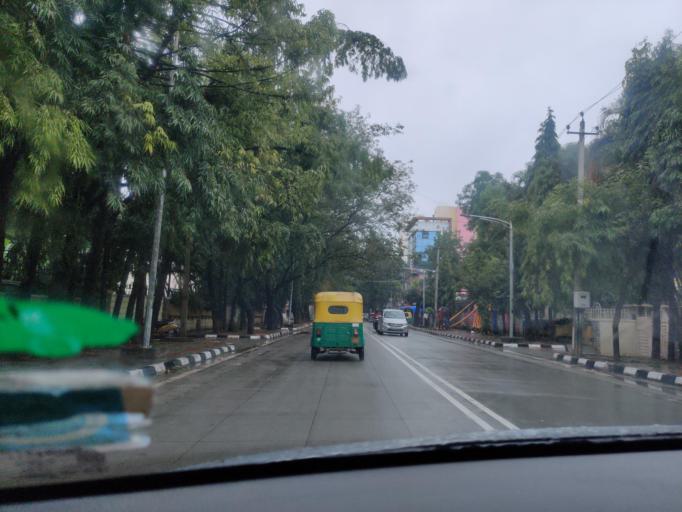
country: IN
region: Karnataka
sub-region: Bangalore Urban
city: Bangalore
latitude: 13.0245
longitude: 77.6321
